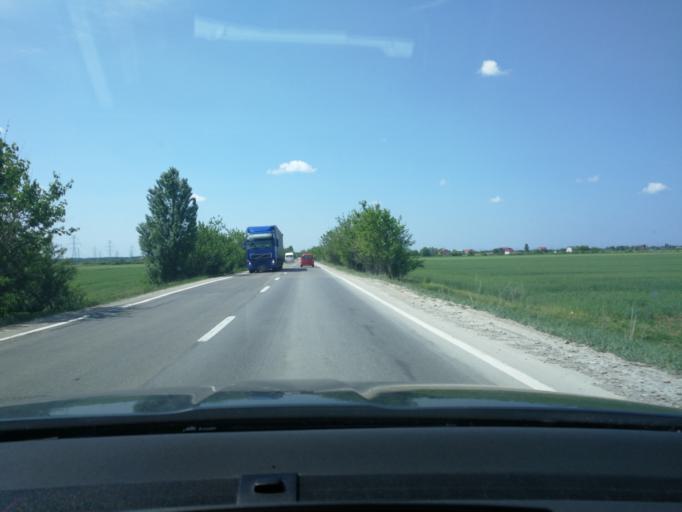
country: RO
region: Prahova
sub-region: Comuna Targsoru Vechi
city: Targsoru Vechi
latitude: 44.8801
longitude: 25.9461
